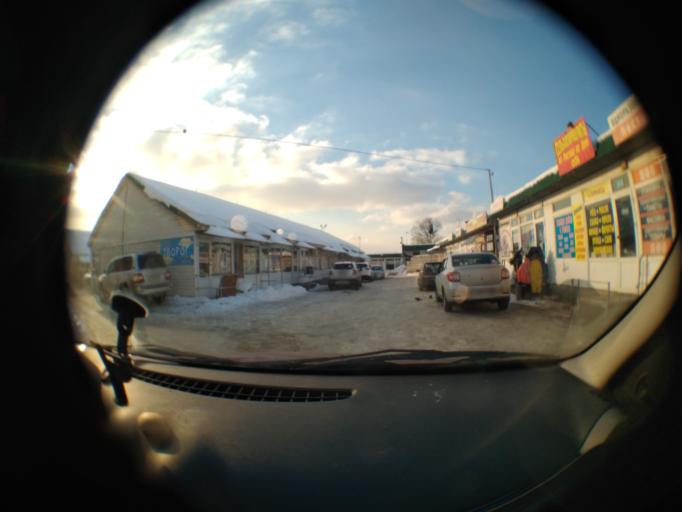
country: RU
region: Moskovskaya
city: Bykovo
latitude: 55.6110
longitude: 38.0876
